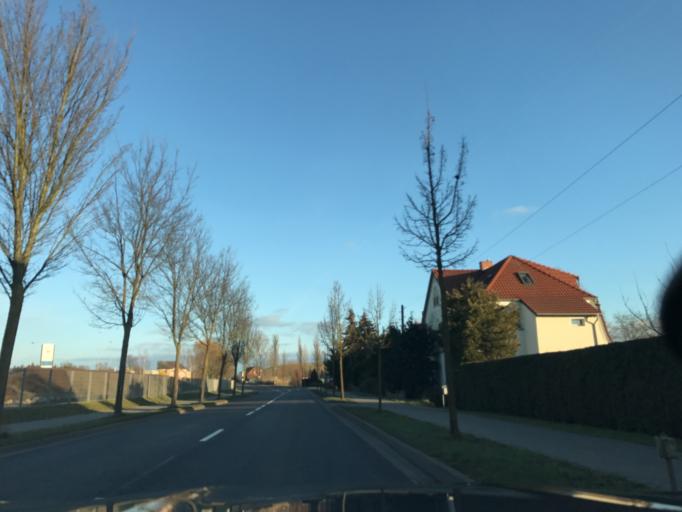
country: DE
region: Saxony-Anhalt
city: Burg bei Magdeburg
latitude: 52.2741
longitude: 11.8800
